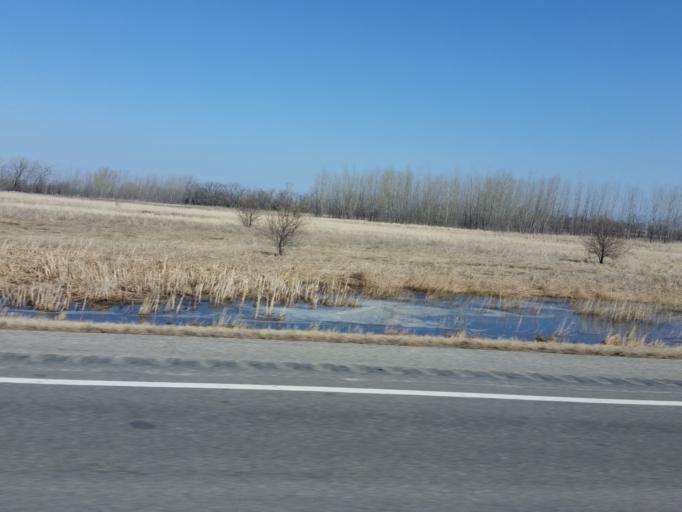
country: US
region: North Dakota
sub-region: Grand Forks County
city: Grand Forks Air Force Base
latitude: 48.1541
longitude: -97.2748
